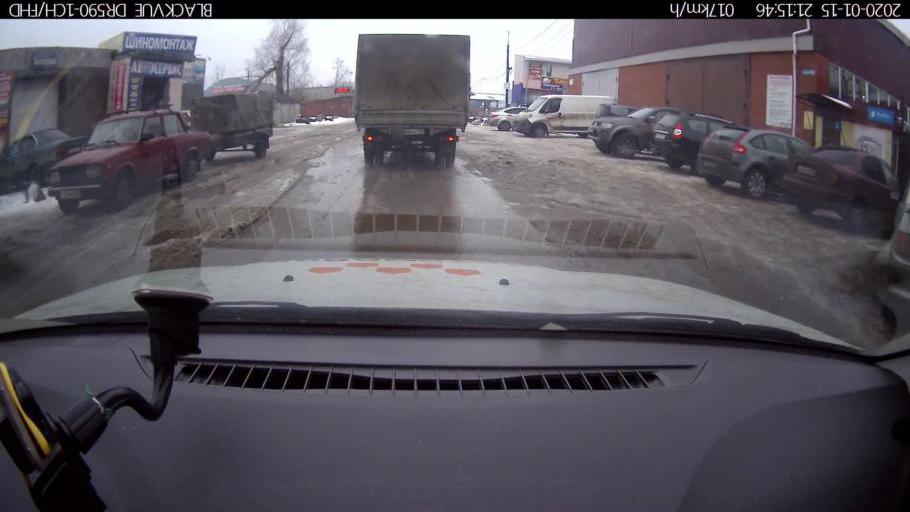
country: RU
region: Nizjnij Novgorod
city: Gorbatovka
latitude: 56.3010
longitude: 43.8610
